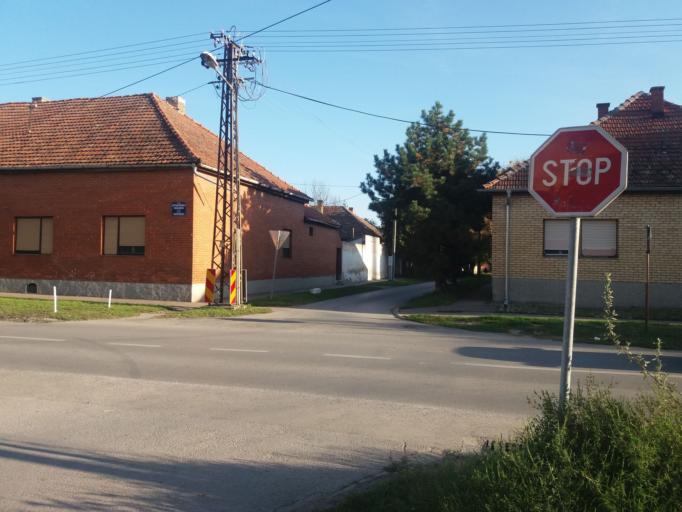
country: RS
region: Autonomna Pokrajina Vojvodina
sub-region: Severnobacki Okrug
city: Subotica
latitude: 46.0917
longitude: 19.6756
